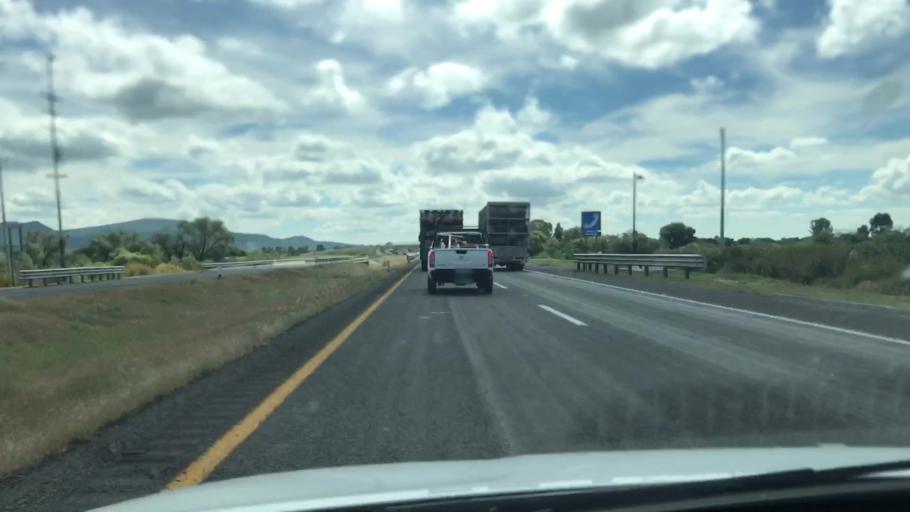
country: MX
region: Guanajuato
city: San Jose Temascatio
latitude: 20.7035
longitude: -101.2670
